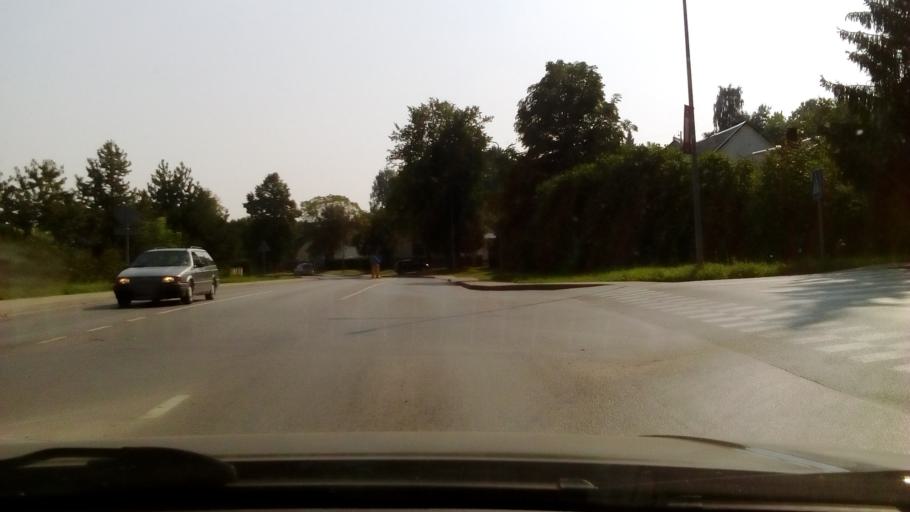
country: LT
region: Alytaus apskritis
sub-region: Alytus
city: Alytus
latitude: 54.4031
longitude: 24.0381
